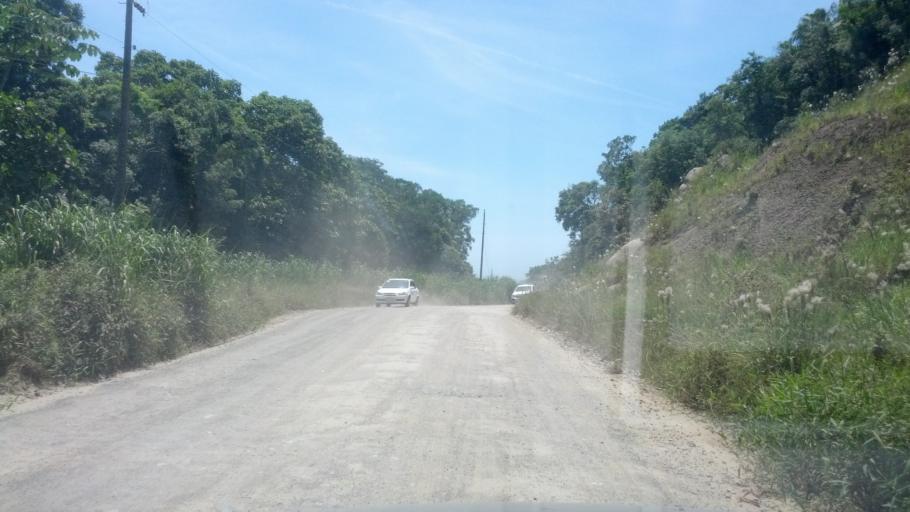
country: BR
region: Santa Catarina
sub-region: Porto Belo
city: Porto Belo
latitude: -27.1624
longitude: -48.5303
